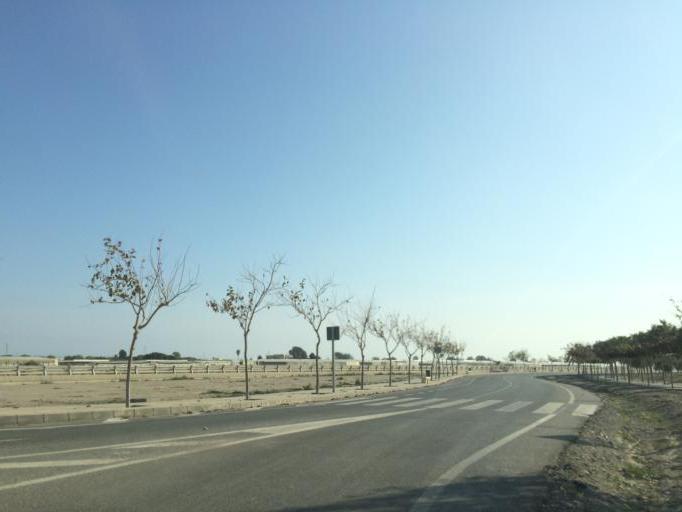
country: ES
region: Andalusia
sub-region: Provincia de Almeria
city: Almeria
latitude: 36.8321
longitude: -2.4286
